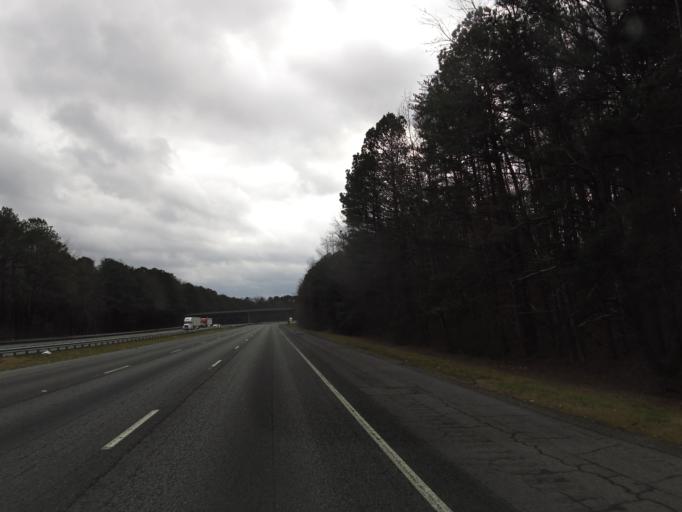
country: US
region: Georgia
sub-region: Whitfield County
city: Dalton
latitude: 34.7424
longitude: -85.0027
